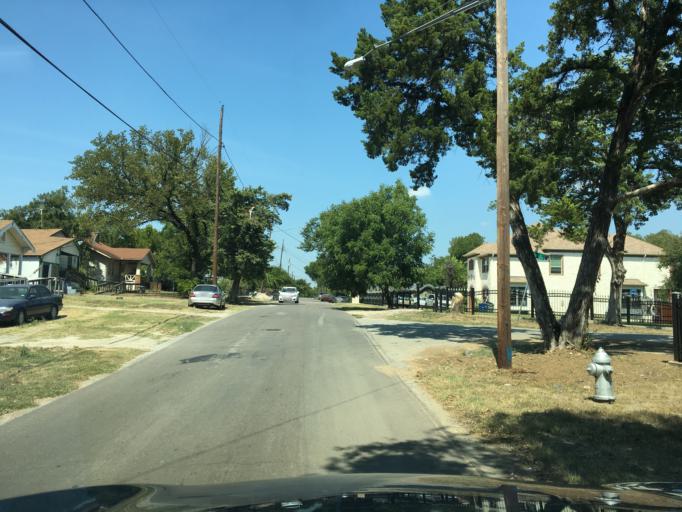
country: US
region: Texas
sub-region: Dallas County
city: Dallas
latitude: 32.7333
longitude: -96.7903
